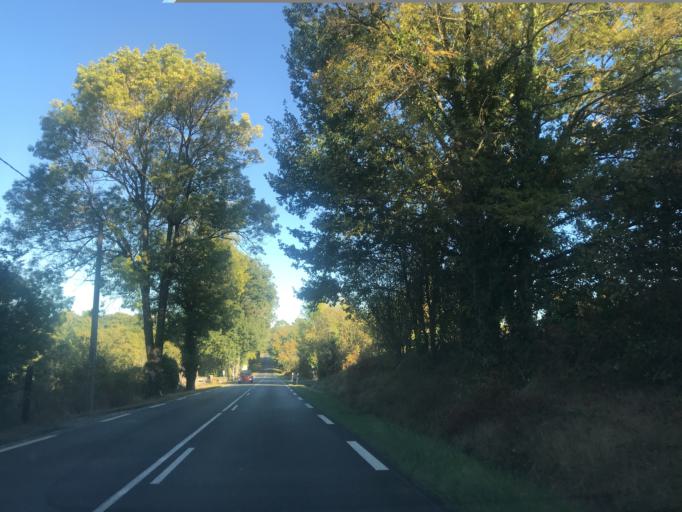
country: FR
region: Poitou-Charentes
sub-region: Departement de la Charente-Maritime
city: Montguyon
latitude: 45.1739
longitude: -0.1071
